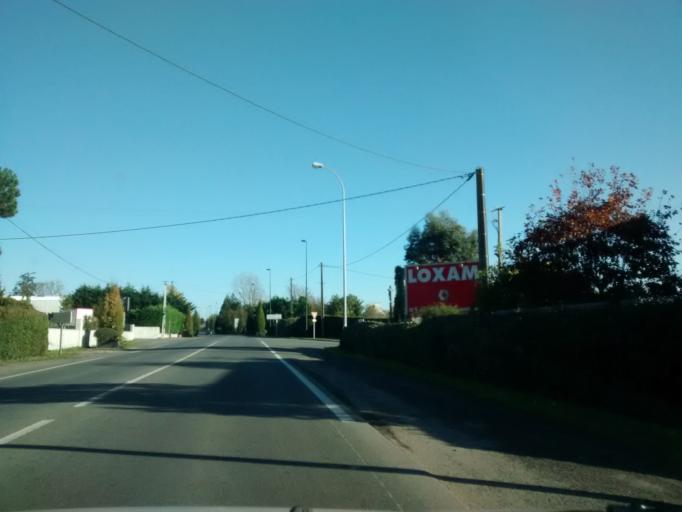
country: FR
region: Brittany
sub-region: Departement des Cotes-d'Armor
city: Ploubezre
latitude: 48.7244
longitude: -3.4364
